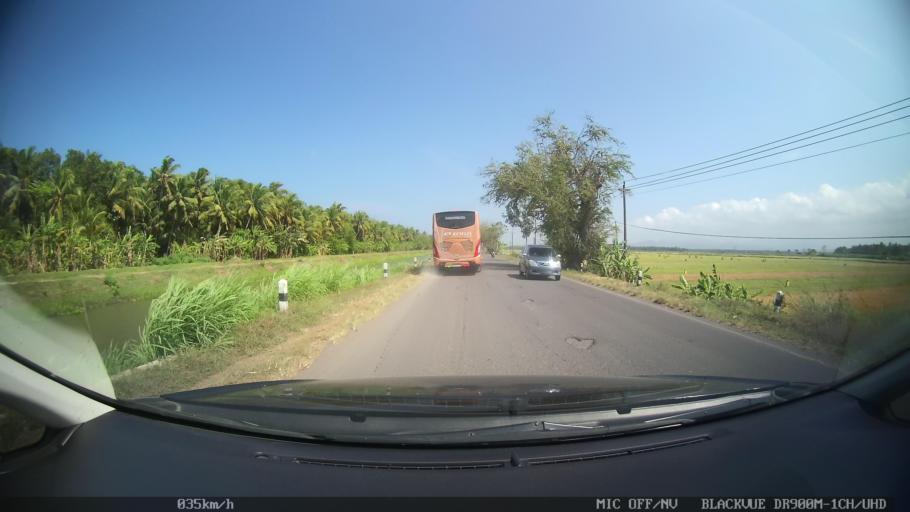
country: ID
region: Daerah Istimewa Yogyakarta
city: Srandakan
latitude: -7.9495
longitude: 110.1848
